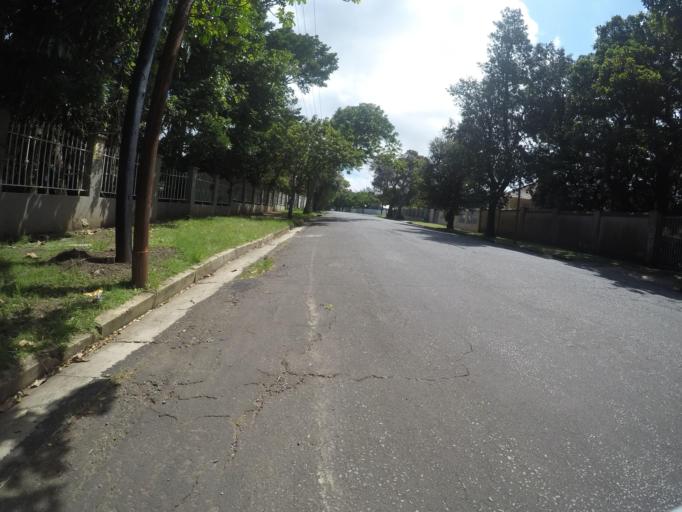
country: ZA
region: Eastern Cape
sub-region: Buffalo City Metropolitan Municipality
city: East London
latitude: -32.9753
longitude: 27.9062
